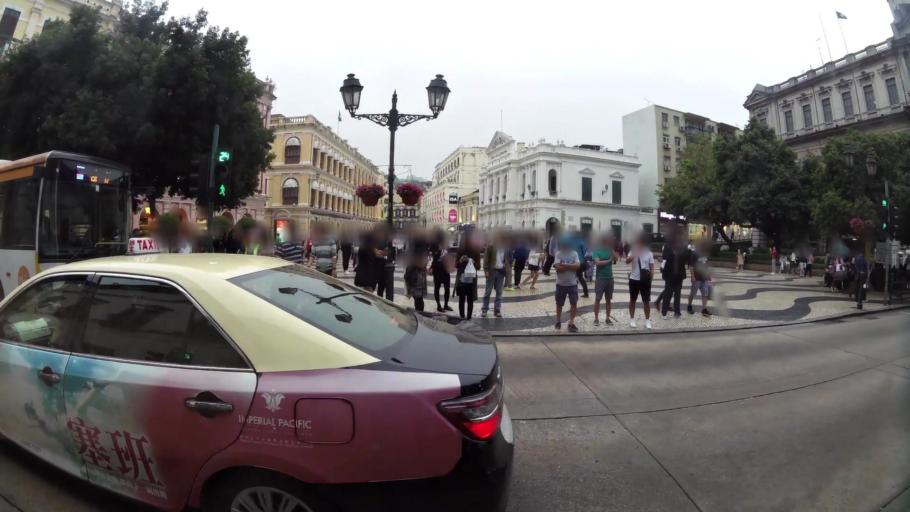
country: MO
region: Macau
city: Macau
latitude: 22.1939
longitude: 113.5399
